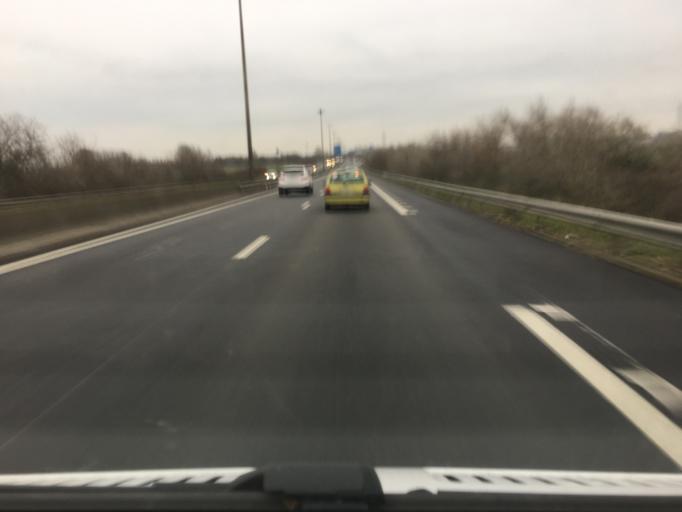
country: FR
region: Nord-Pas-de-Calais
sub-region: Departement du Nord
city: Bourbourg
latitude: 50.9588
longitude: 2.1751
